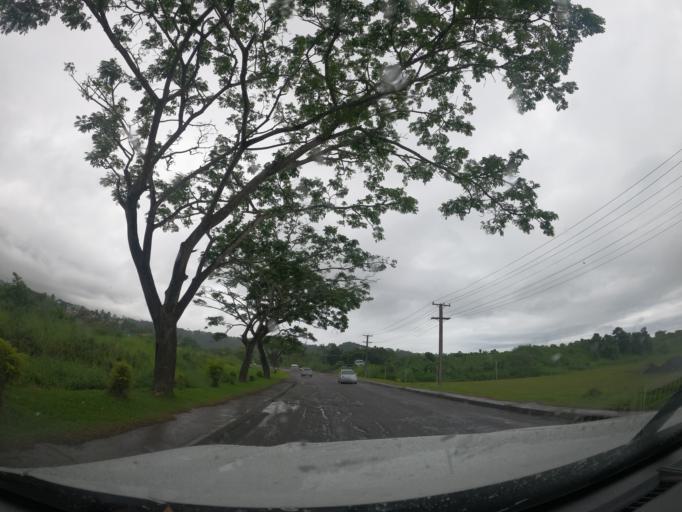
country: FJ
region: Central
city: Suva
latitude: -18.1135
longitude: 178.4256
